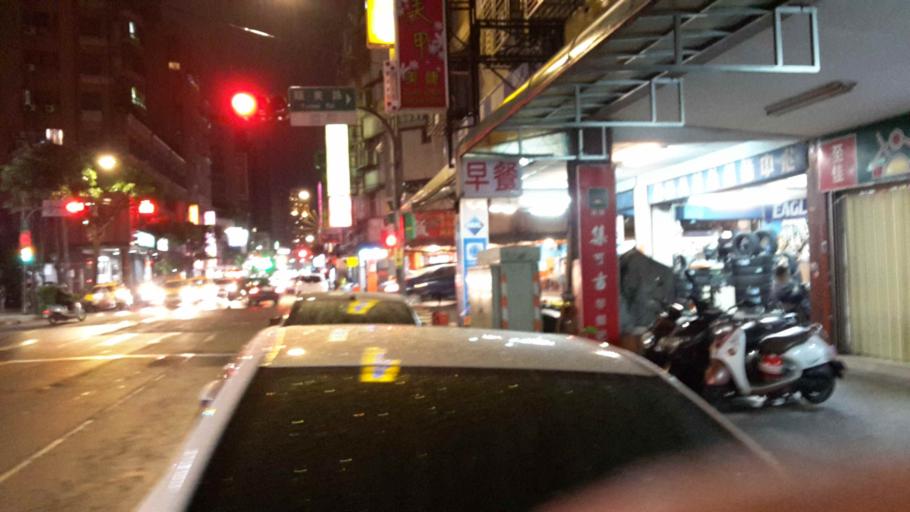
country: TW
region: Taipei
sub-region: Taipei
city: Banqiao
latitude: 25.0057
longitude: 121.4993
